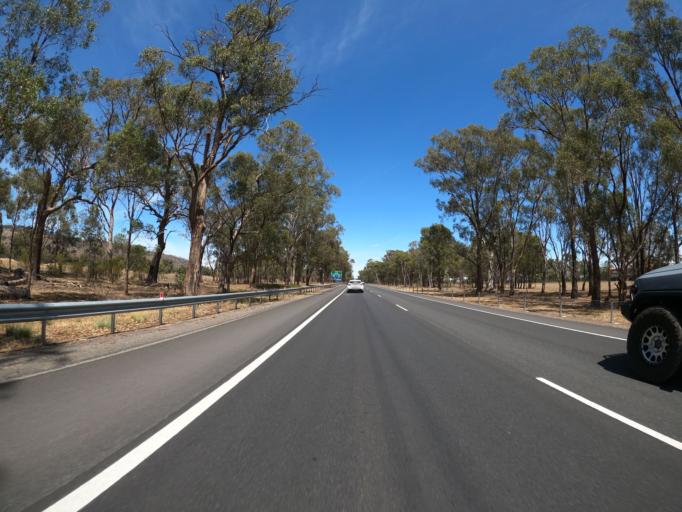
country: AU
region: Victoria
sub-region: Greater Shepparton
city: Shepparton
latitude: -36.7346
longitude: 145.6021
